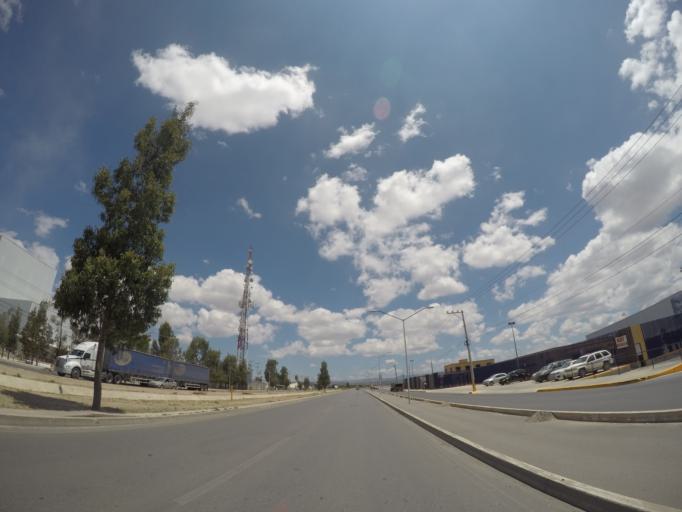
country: MX
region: San Luis Potosi
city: La Pila
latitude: 22.0508
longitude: -100.8659
